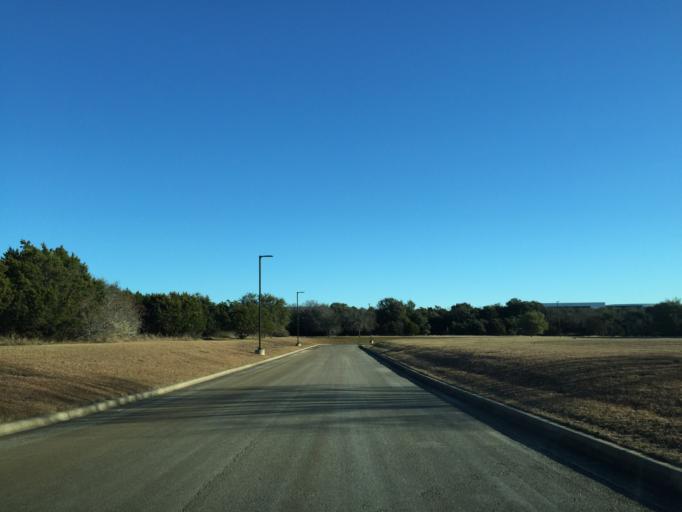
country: US
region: Texas
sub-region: Williamson County
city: Jollyville
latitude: 30.4235
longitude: -97.7461
